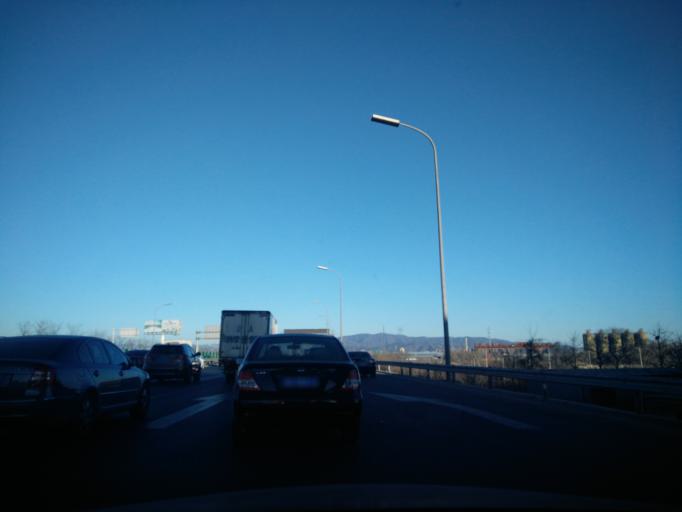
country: CN
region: Beijing
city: Lugu
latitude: 39.8683
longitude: 116.2052
